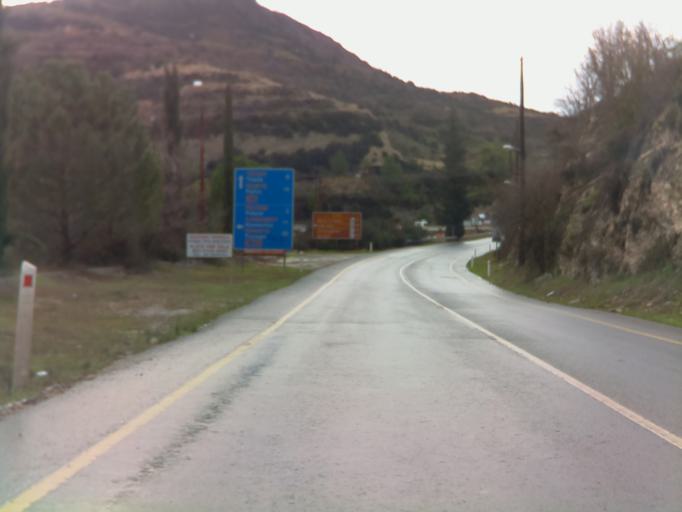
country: CY
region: Pafos
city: Tala
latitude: 34.8797
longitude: 32.4824
